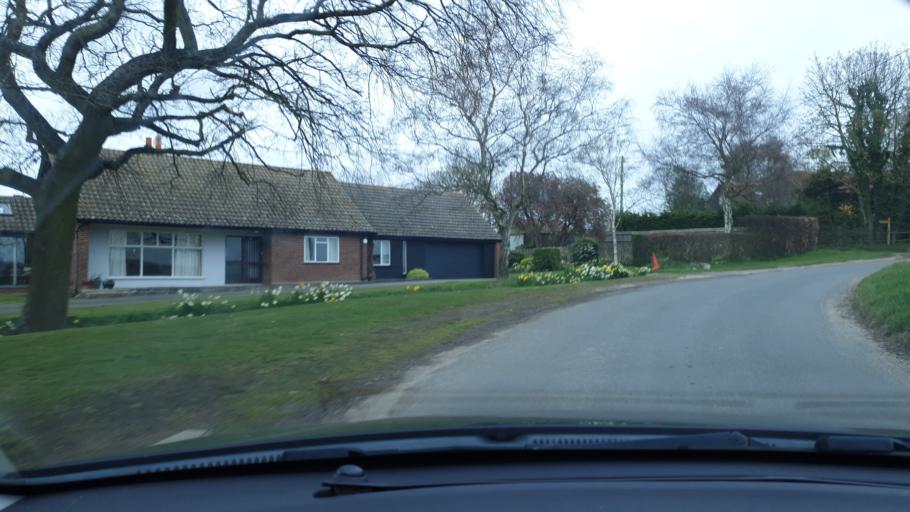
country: GB
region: England
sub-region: Essex
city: Mistley
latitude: 51.9431
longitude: 1.1578
